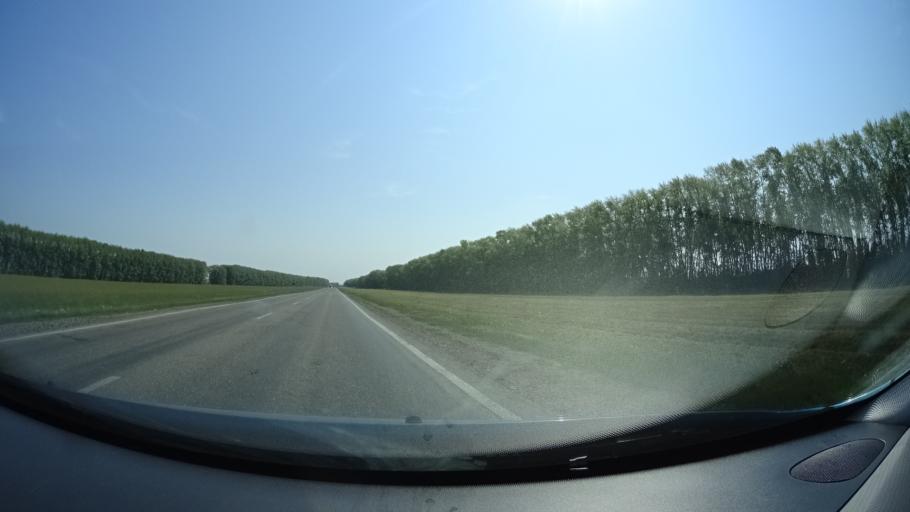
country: RU
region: Bashkortostan
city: Karmaskaly
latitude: 54.3959
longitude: 56.1072
